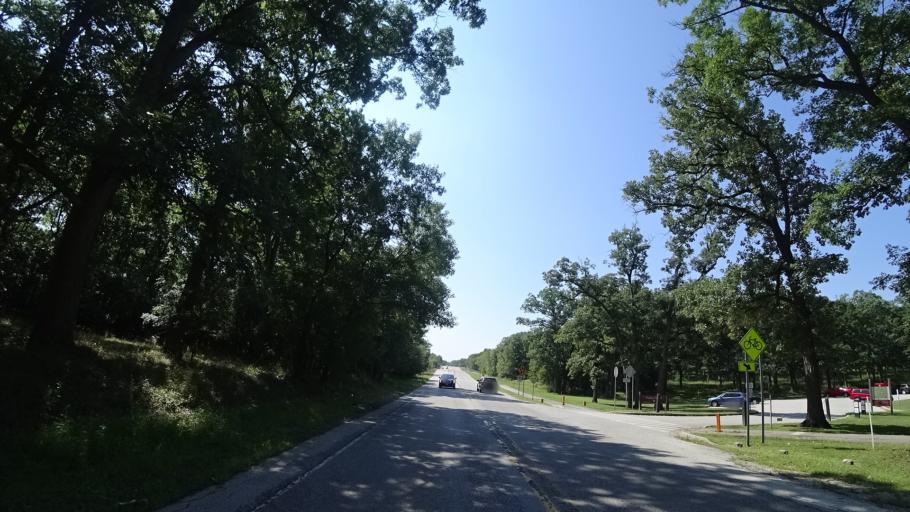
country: US
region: Illinois
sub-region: Cook County
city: Oak Forest
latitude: 41.5929
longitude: -87.7557
